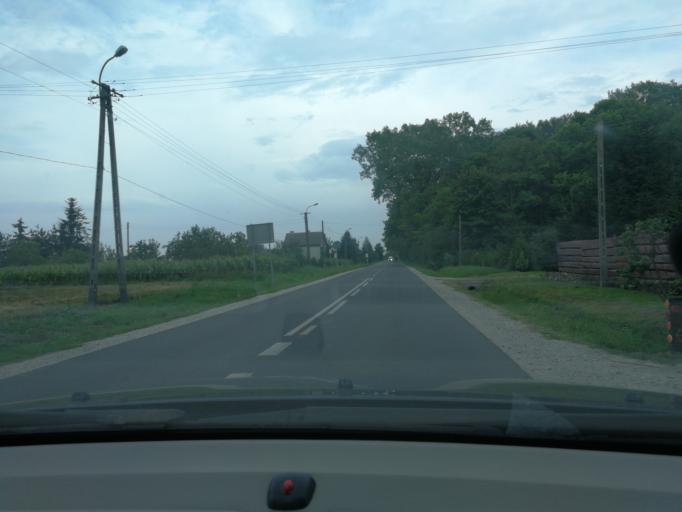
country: PL
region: Masovian Voivodeship
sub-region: Powiat warszawski zachodni
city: Bieniewice
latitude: 52.1196
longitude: 20.5681
